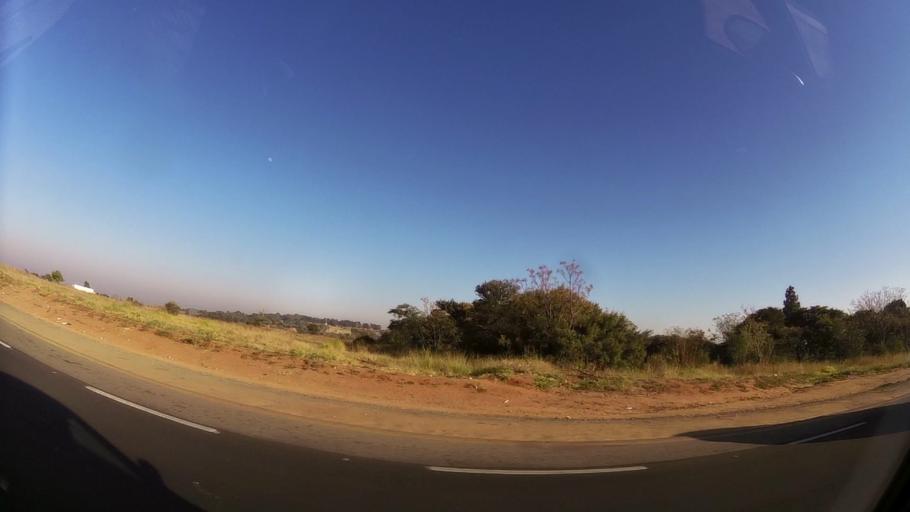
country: ZA
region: Gauteng
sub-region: City of Johannesburg Metropolitan Municipality
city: Midrand
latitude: -25.9387
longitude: 28.0954
